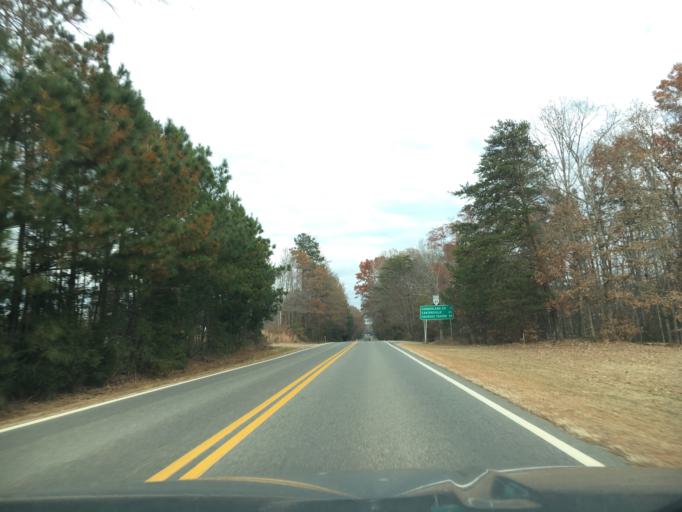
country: US
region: Virginia
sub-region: Cumberland County
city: Cumberland
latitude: 37.4329
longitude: -78.3350
